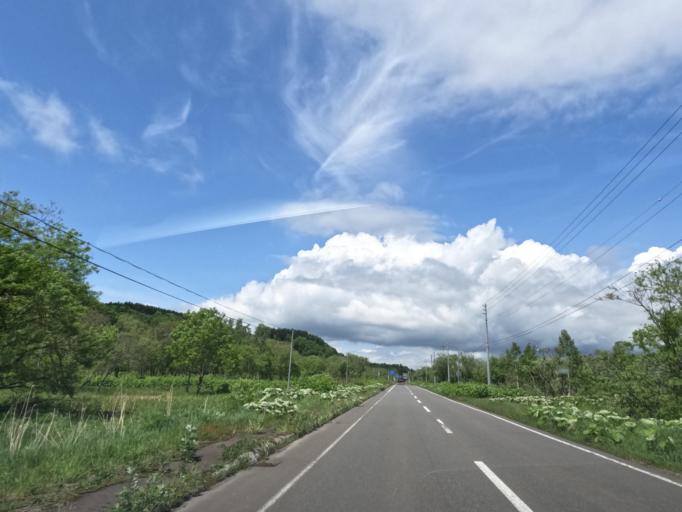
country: JP
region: Hokkaido
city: Tobetsu
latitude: 43.3941
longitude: 141.5798
